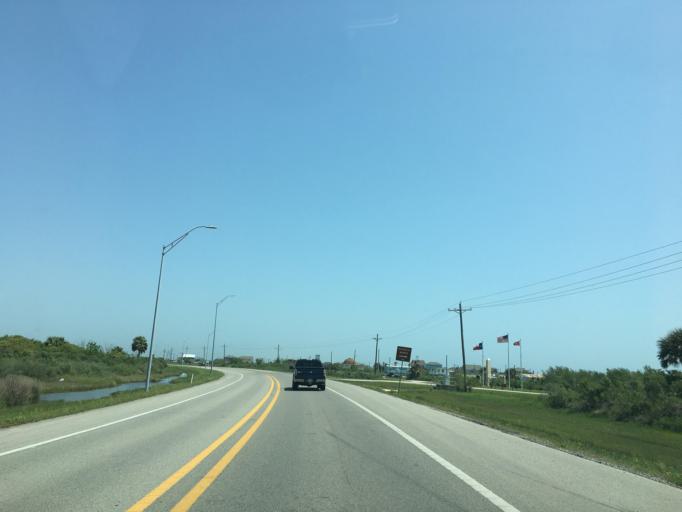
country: US
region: Texas
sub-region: Galveston County
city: Galveston
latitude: 29.3677
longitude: -94.7596
